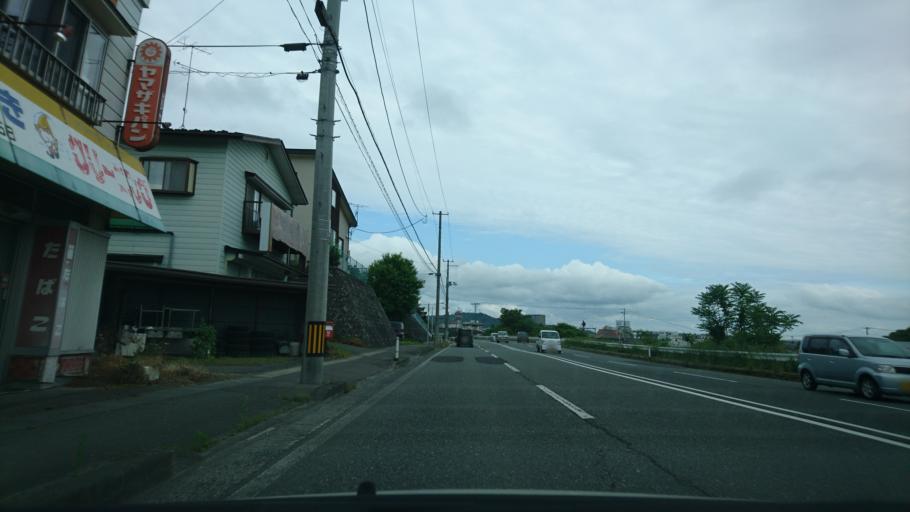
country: JP
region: Iwate
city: Ichinoseki
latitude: 38.9192
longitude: 141.1401
